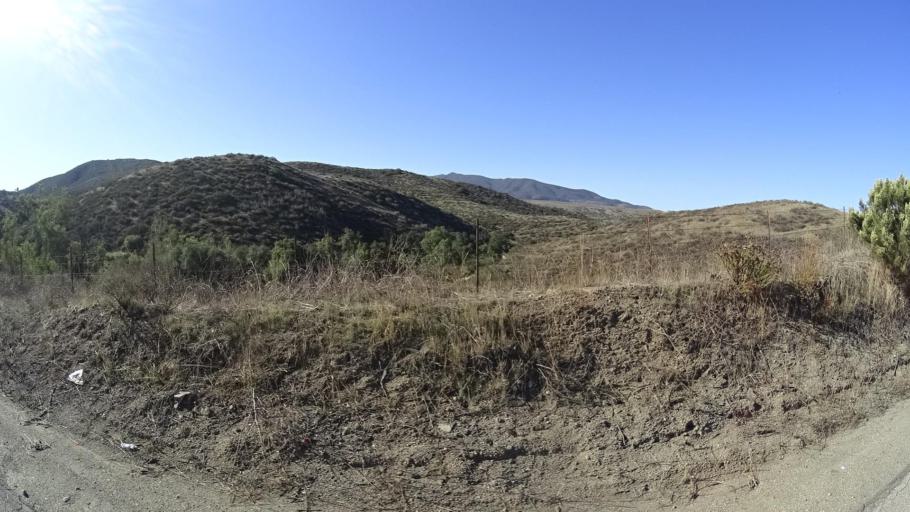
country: US
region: California
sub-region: San Diego County
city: Jamul
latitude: 32.6727
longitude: -116.8057
